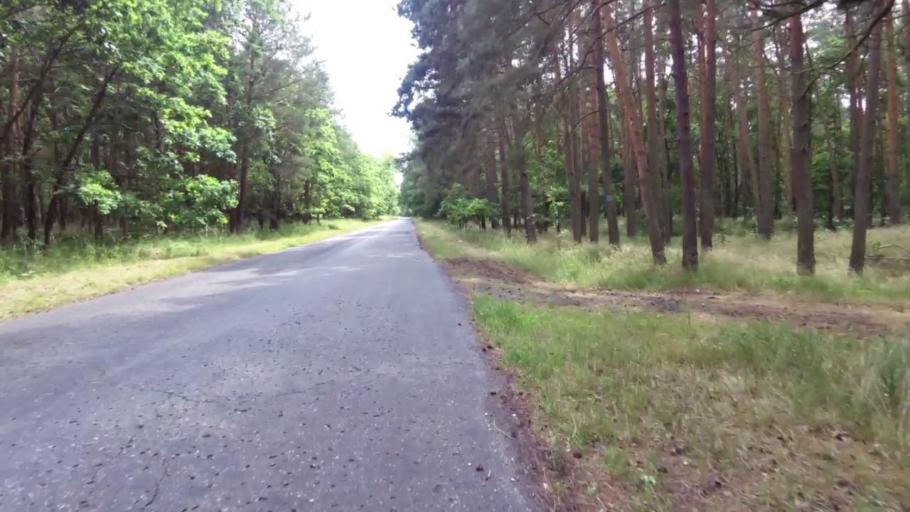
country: PL
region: West Pomeranian Voivodeship
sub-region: Powiat goleniowski
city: Stepnica
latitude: 53.7111
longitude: 14.5521
